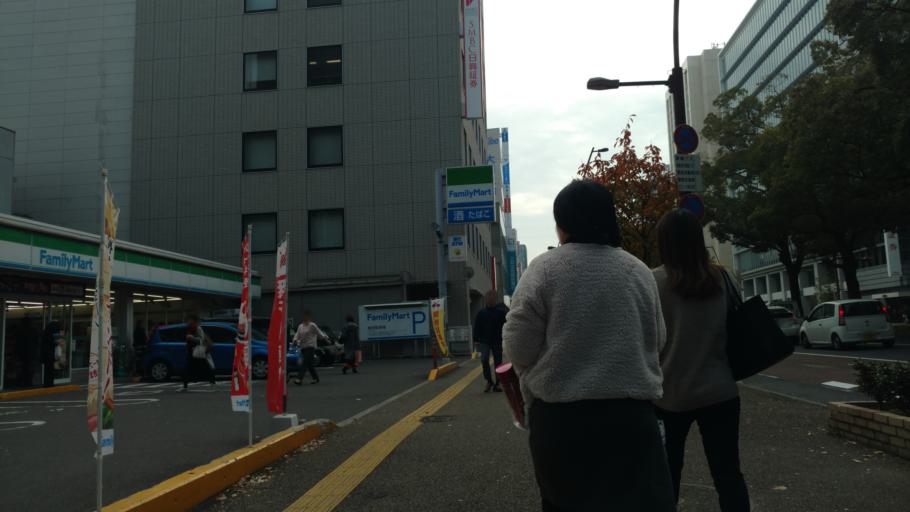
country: JP
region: Kagawa
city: Takamatsu-shi
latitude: 34.3451
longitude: 134.0484
